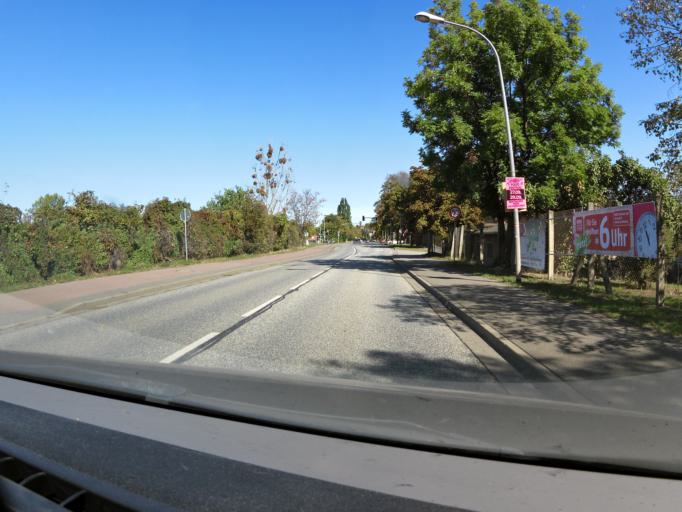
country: DE
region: Saxony-Anhalt
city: Quedlinburg
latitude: 51.7766
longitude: 11.1412
